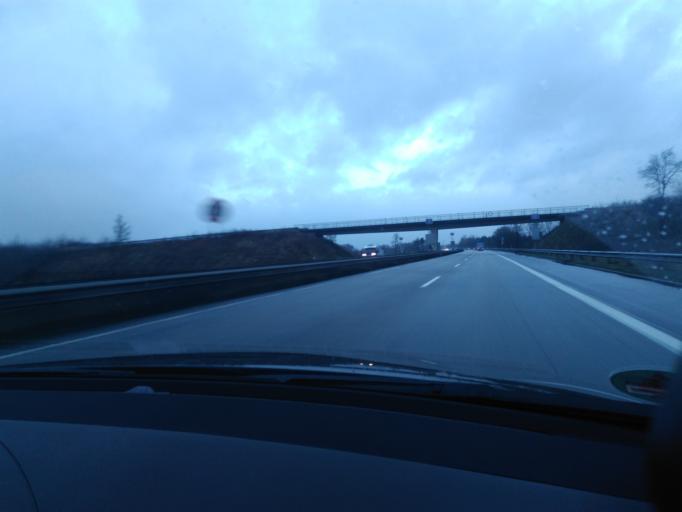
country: DE
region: Schleswig-Holstein
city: Padenstedt
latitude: 54.0311
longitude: 9.9326
